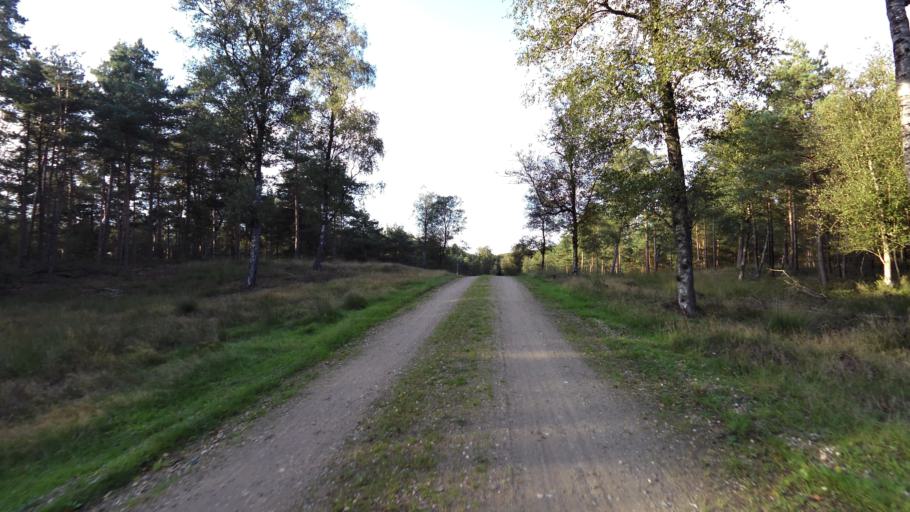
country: NL
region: Gelderland
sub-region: Gemeente Apeldoorn
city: Uddel
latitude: 52.2880
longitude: 5.8676
